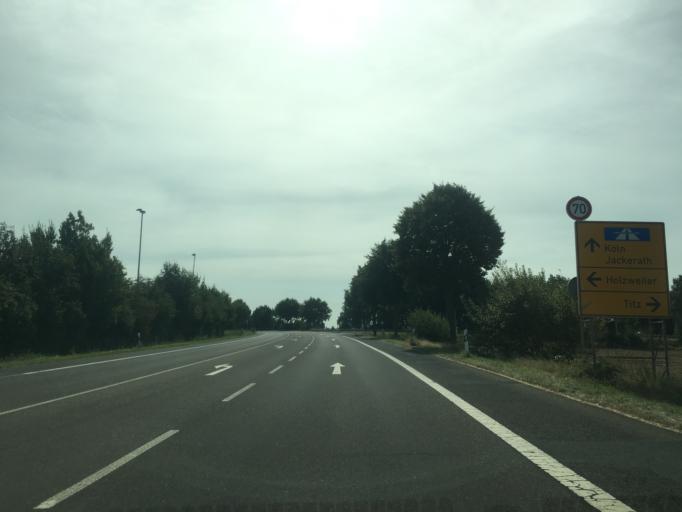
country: DE
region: North Rhine-Westphalia
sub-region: Regierungsbezirk Koln
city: Titz
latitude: 51.0448
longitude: 6.3949
